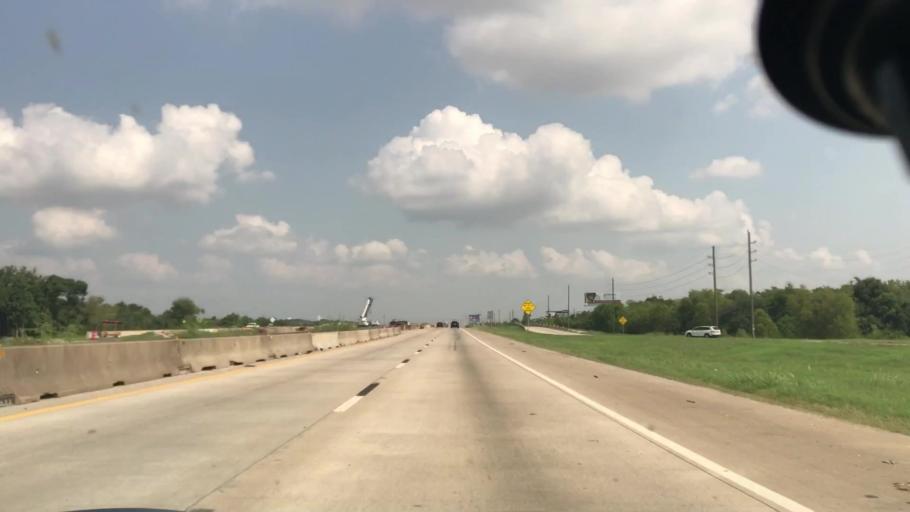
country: US
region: Texas
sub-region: Brazoria County
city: Iowa Colony
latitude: 29.5263
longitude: -95.3866
